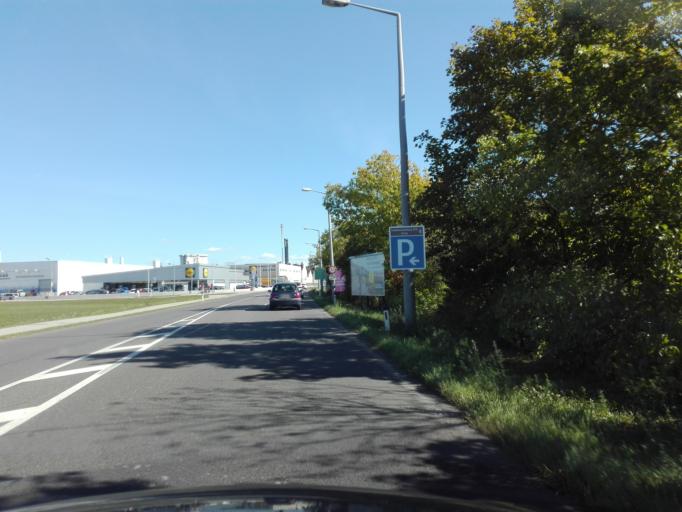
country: AT
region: Upper Austria
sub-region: Politischer Bezirk Linz-Land
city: Enns
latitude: 48.2158
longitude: 14.4672
